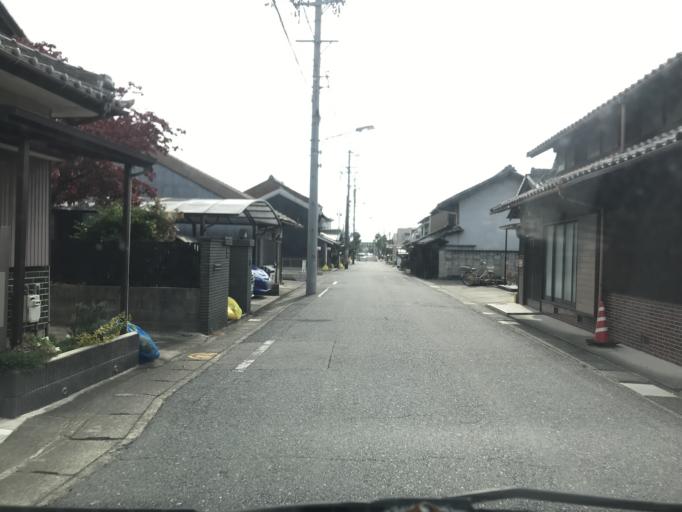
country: JP
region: Aichi
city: Inazawa
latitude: 35.2097
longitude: 136.8398
